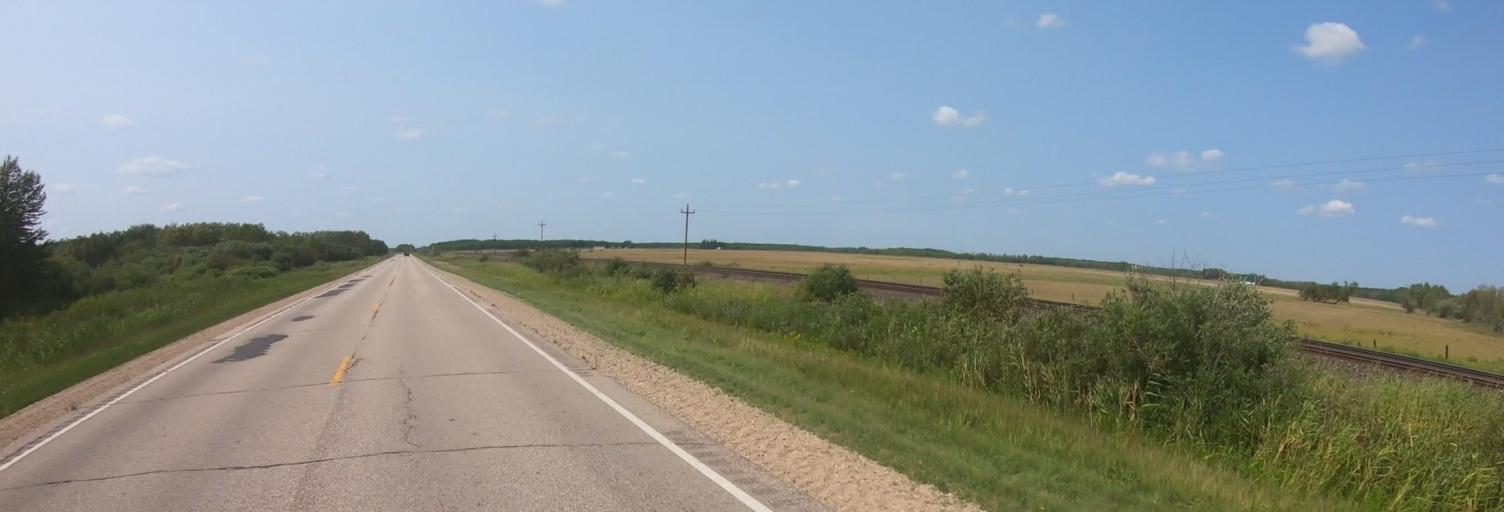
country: US
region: Minnesota
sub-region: Lake of the Woods County
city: Baudette
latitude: 48.7341
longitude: -94.8109
